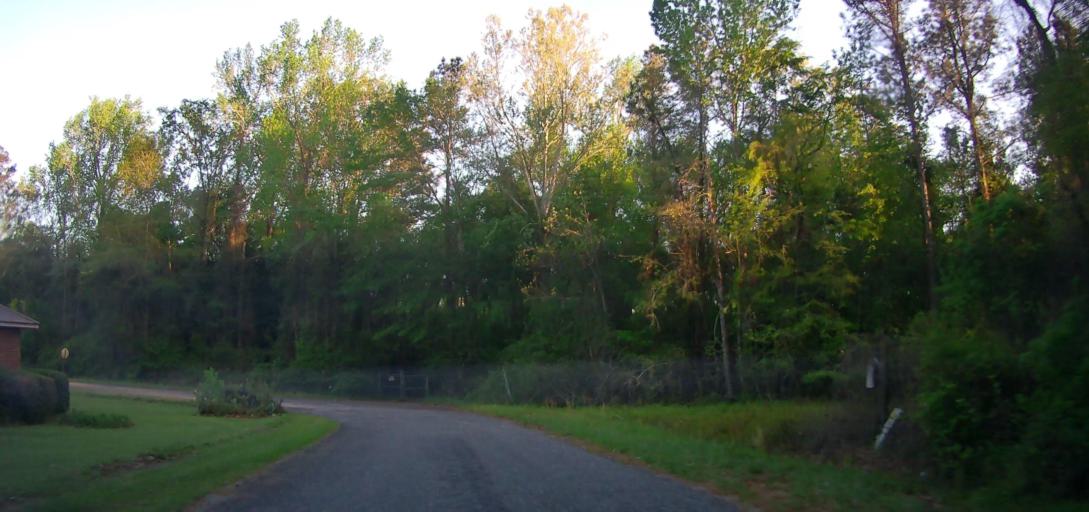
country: US
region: Georgia
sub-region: Talbot County
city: Talbotton
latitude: 32.5352
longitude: -84.6028
